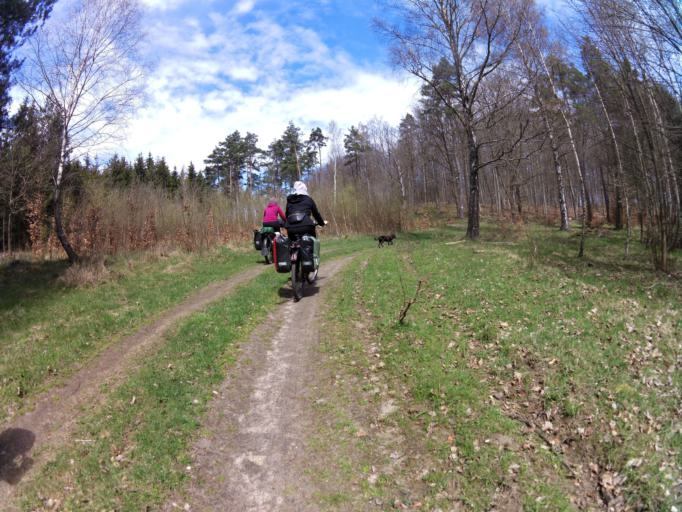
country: PL
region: West Pomeranian Voivodeship
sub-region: Powiat szczecinecki
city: Szczecinek
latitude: 53.7801
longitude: 16.6183
